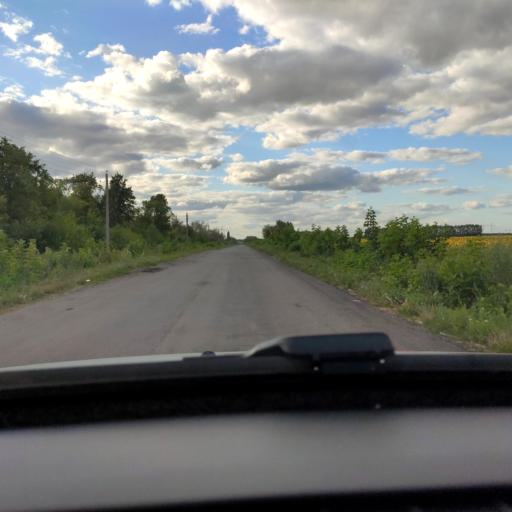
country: RU
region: Voronezj
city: Orlovo
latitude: 51.6812
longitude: 39.6781
